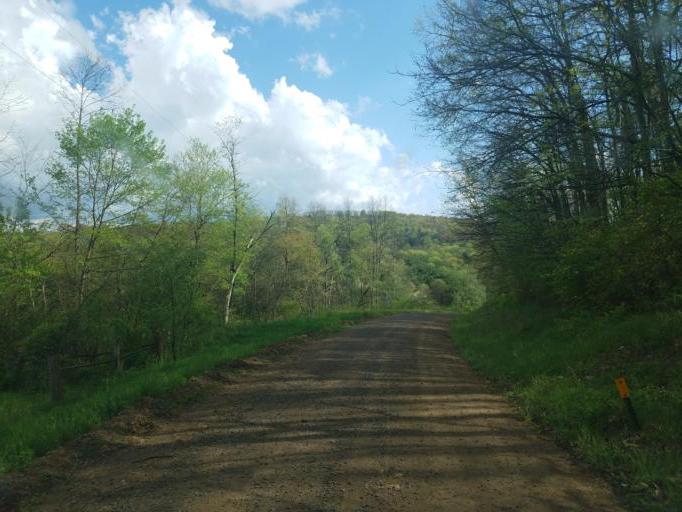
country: US
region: Ohio
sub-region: Knox County
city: Oak Hill
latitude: 40.4155
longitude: -82.2126
